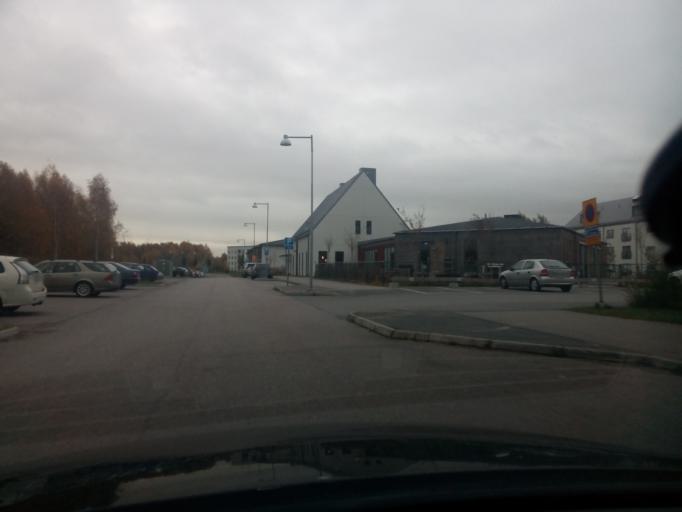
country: SE
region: Soedermanland
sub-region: Nykopings Kommun
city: Nykoping
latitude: 58.7469
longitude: 17.0421
